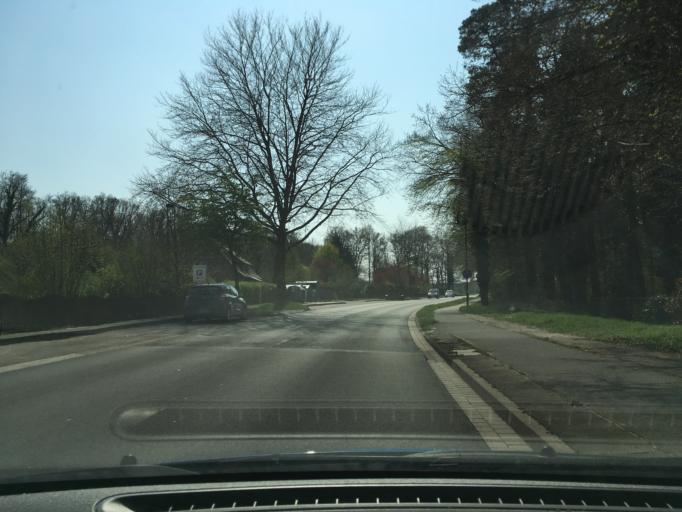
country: DE
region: Lower Saxony
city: Vogelsen
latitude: 53.2876
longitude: 10.3673
